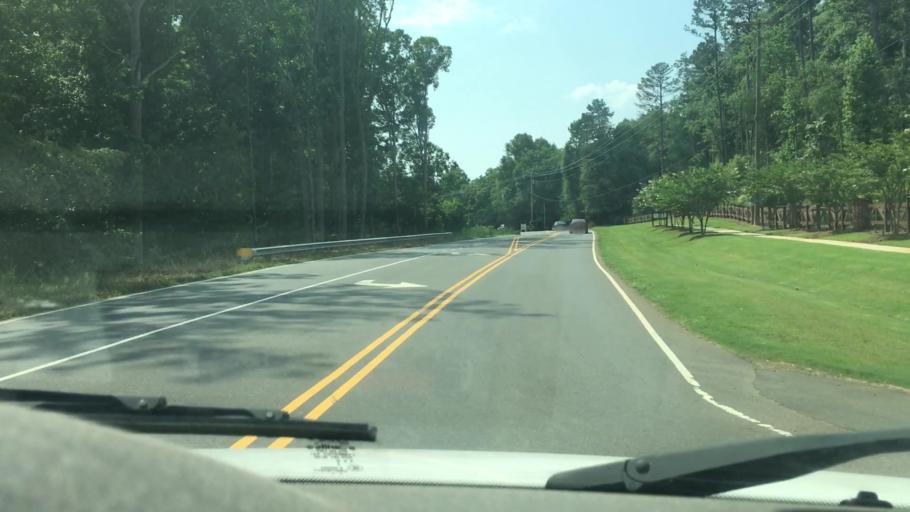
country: US
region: North Carolina
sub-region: Mecklenburg County
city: Huntersville
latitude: 35.4060
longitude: -80.8848
